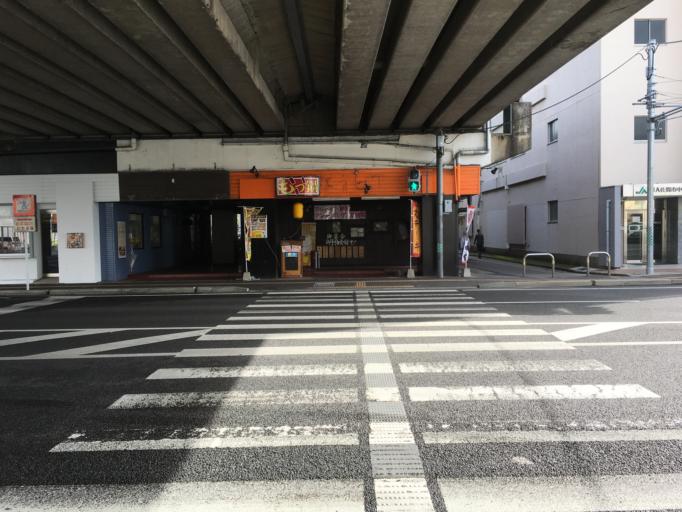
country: JP
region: Saga Prefecture
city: Saga-shi
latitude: 33.2643
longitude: 130.3000
